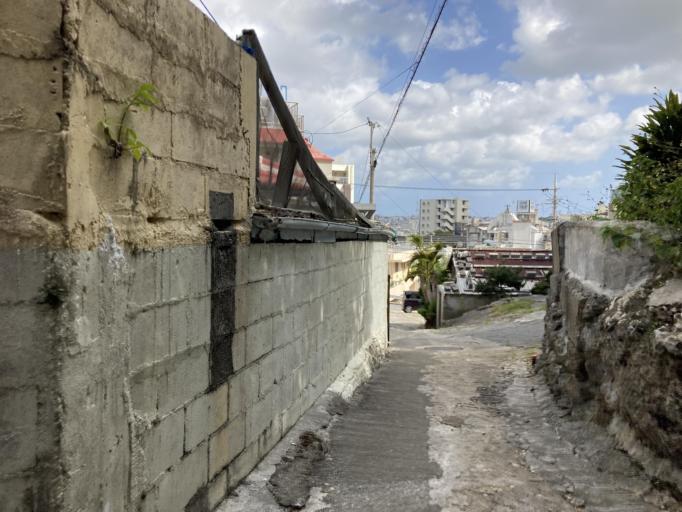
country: JP
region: Okinawa
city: Naha-shi
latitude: 26.2008
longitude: 127.6720
